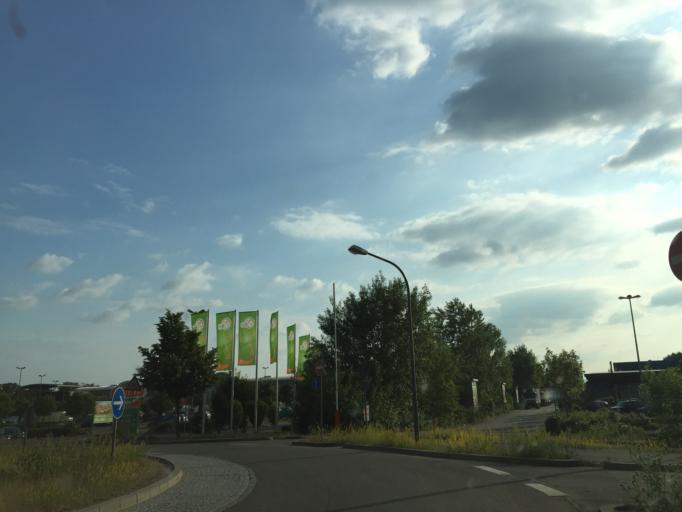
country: DE
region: Rheinland-Pfalz
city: Frankenthal
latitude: 49.4881
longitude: 8.3515
